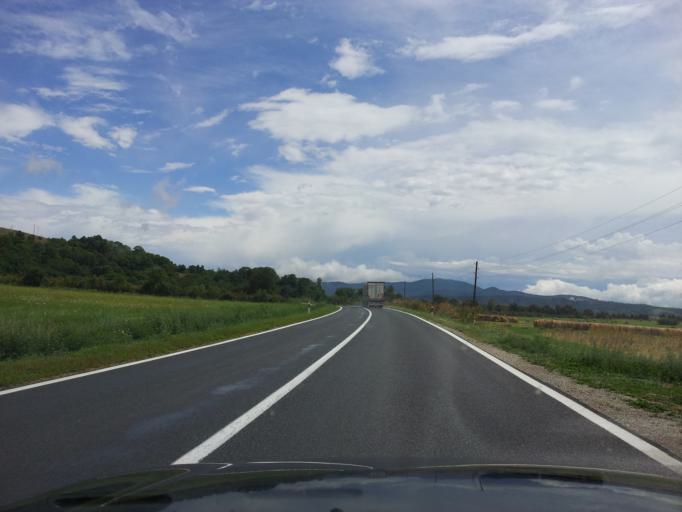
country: BA
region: Federation of Bosnia and Herzegovina
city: Bihac
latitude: 44.5795
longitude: 15.7450
